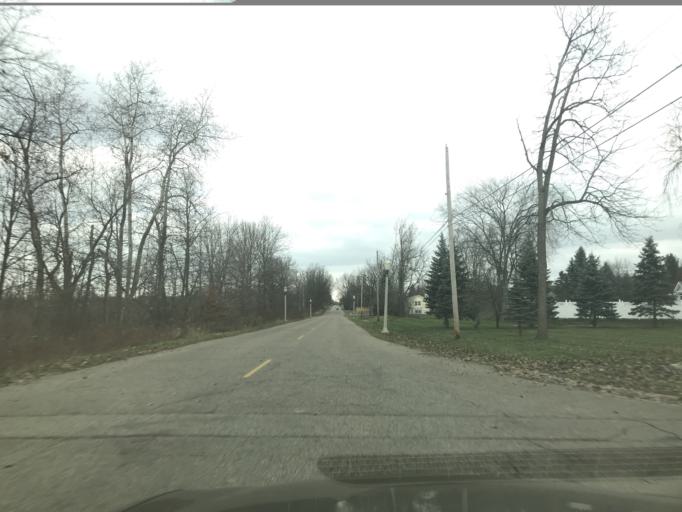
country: US
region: Michigan
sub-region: Eaton County
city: Waverly
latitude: 42.7205
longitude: -84.6817
